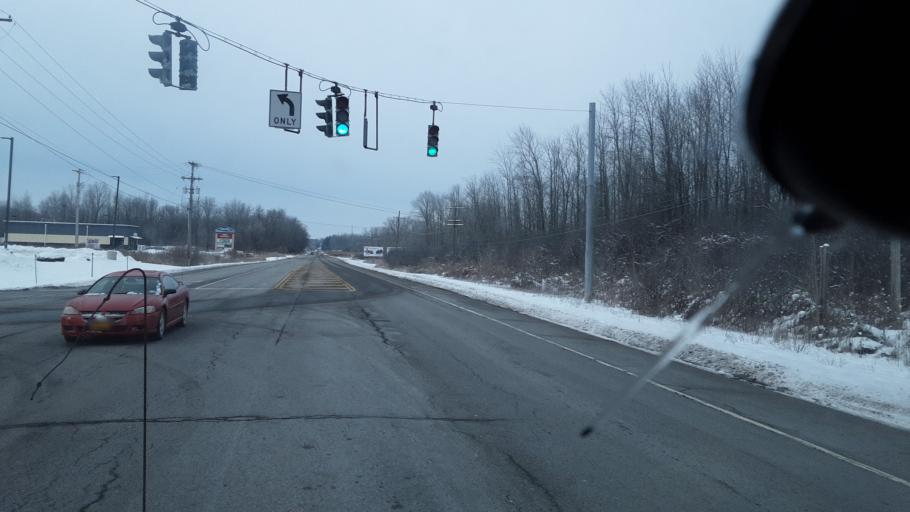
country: US
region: New York
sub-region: Wayne County
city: Newark
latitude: 43.0536
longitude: -77.0592
